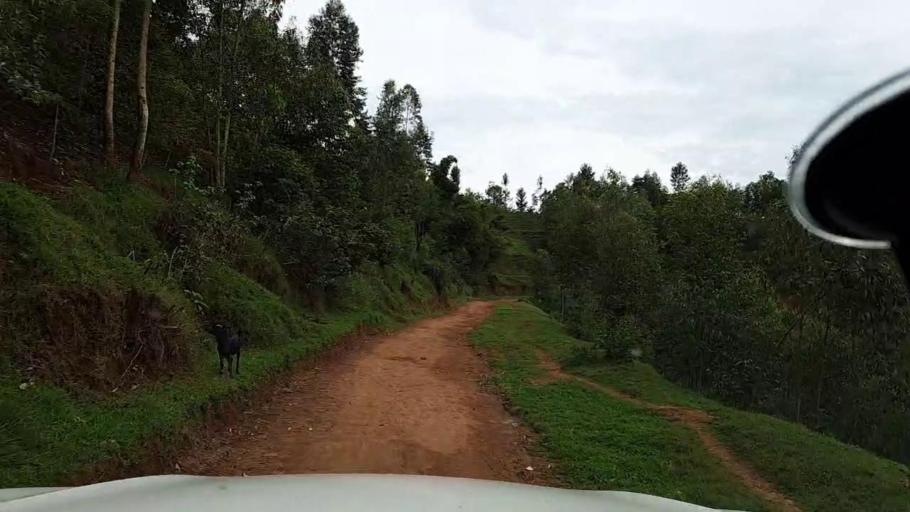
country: RW
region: Southern Province
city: Gitarama
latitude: -2.1221
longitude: 29.6492
